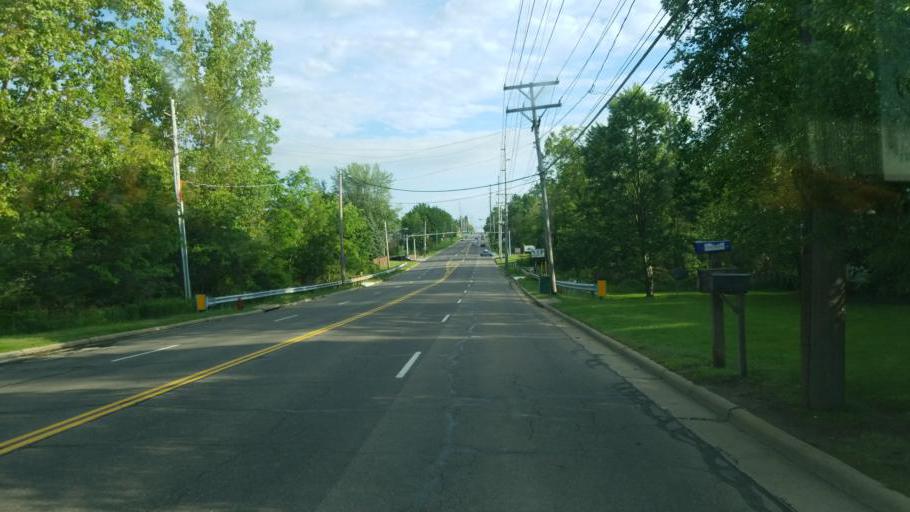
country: US
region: Ohio
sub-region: Summit County
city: Stow
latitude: 41.1962
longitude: -81.4405
